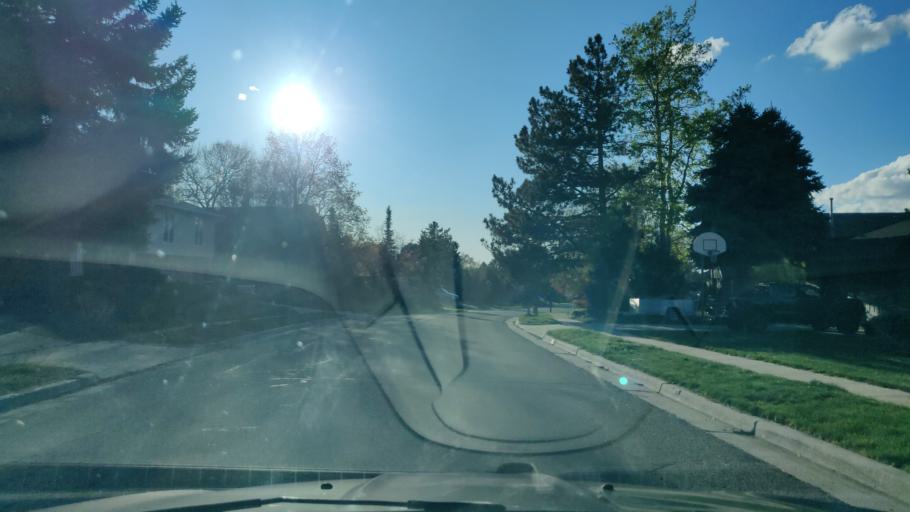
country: US
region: Utah
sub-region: Salt Lake County
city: Cottonwood Heights
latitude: 40.6184
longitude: -111.7984
